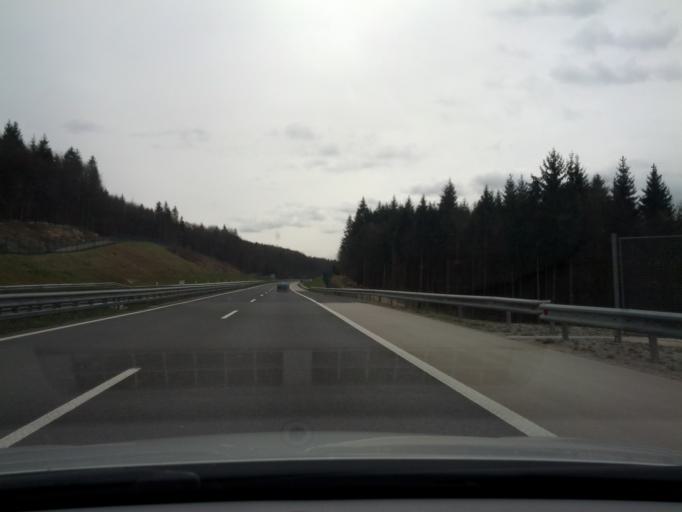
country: SI
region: Mirna Pec
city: Mirna Pec
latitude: 45.8882
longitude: 15.0651
